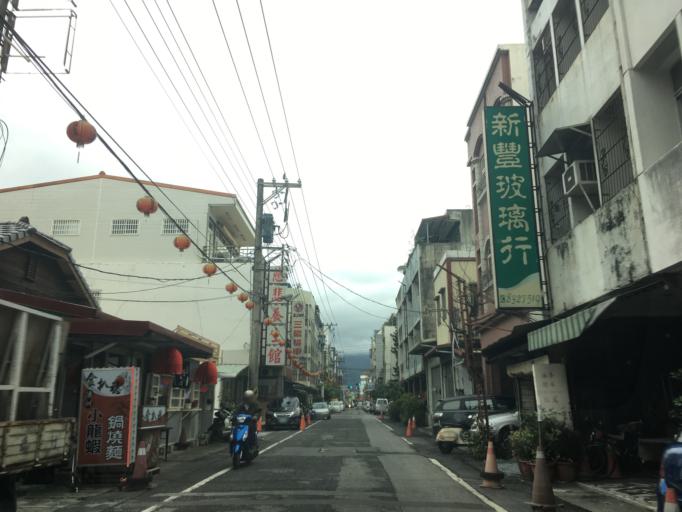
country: TW
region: Taiwan
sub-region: Hualien
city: Hualian
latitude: 23.9742
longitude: 121.6054
